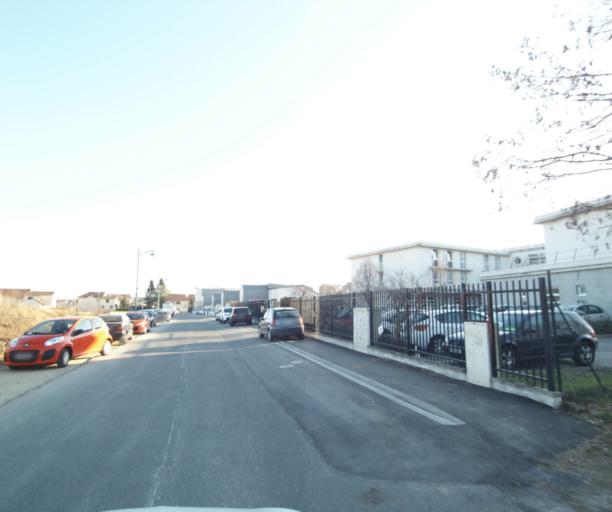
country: FR
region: Lorraine
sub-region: Departement de Meurthe-et-Moselle
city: Malzeville
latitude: 48.7152
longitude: 6.1759
